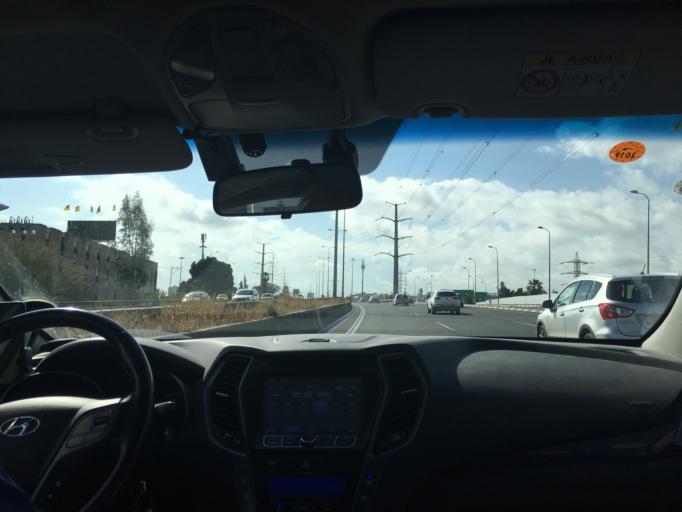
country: IL
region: Tel Aviv
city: Giv`at Shemu'el
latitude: 32.0957
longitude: 34.8460
